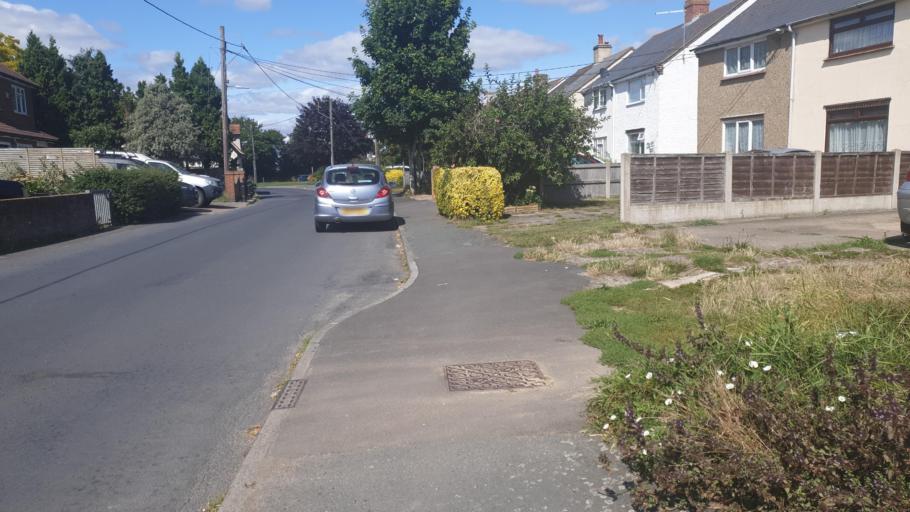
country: GB
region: England
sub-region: Essex
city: Dovercourt
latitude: 51.9174
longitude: 1.2224
